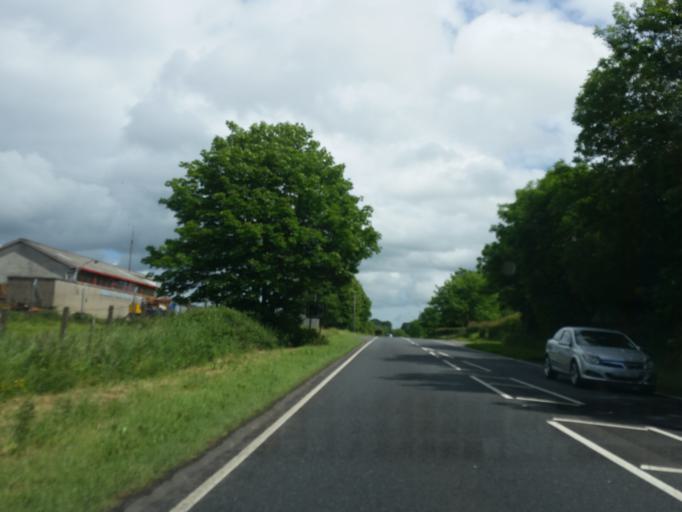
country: IE
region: Ulster
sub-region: County Monaghan
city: Monaghan
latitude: 54.4740
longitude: -7.0646
